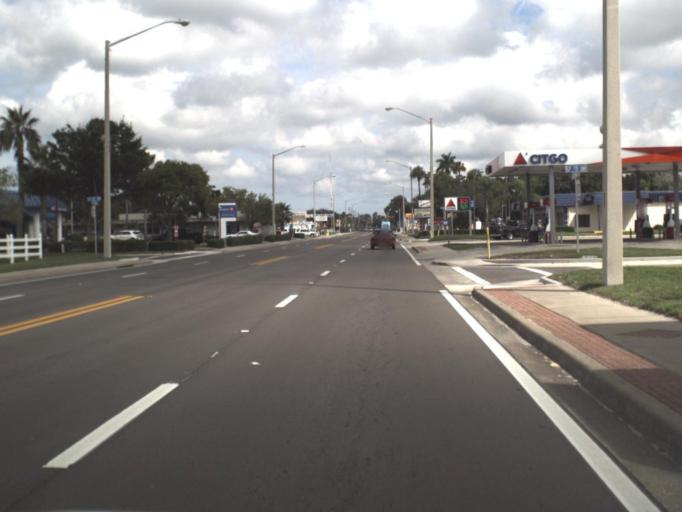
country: US
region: Florida
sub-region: Manatee County
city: Palmetto
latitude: 27.5243
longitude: -82.5729
